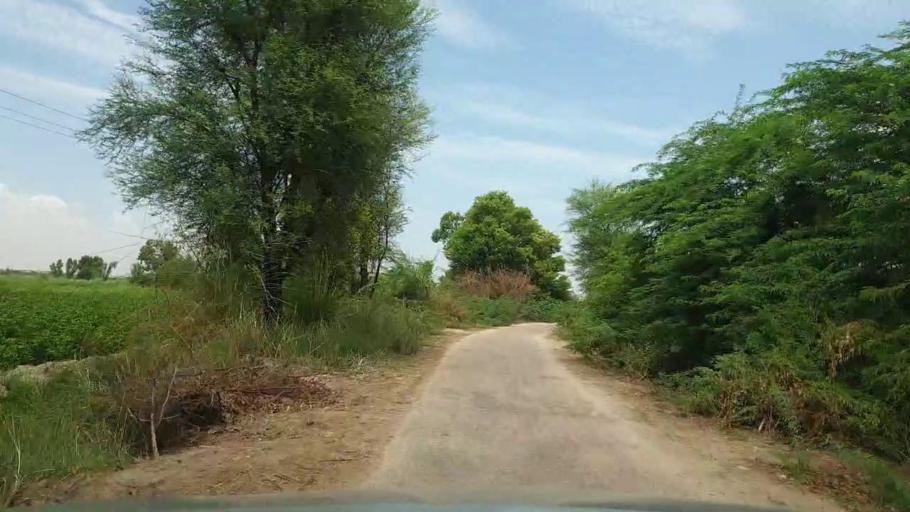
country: PK
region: Sindh
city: Bozdar
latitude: 27.0155
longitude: 68.9407
